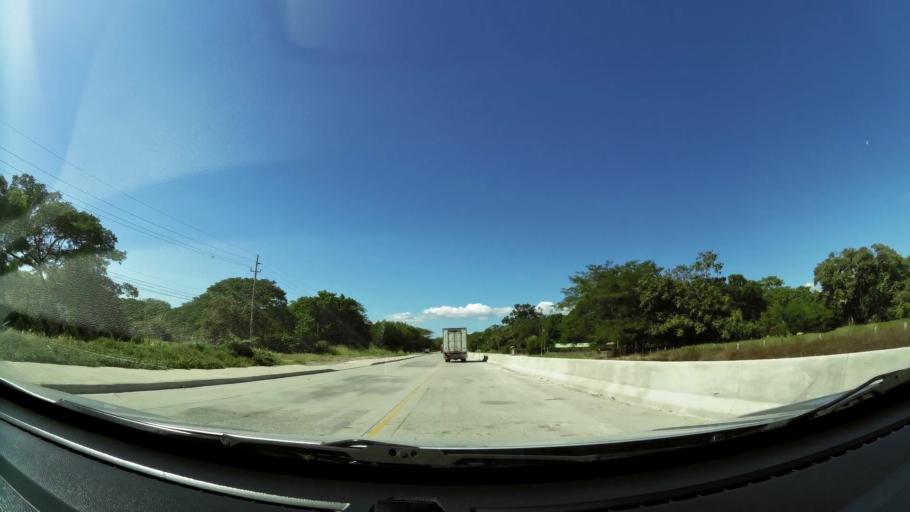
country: CR
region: Guanacaste
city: Liberia
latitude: 10.5769
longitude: -85.4028
